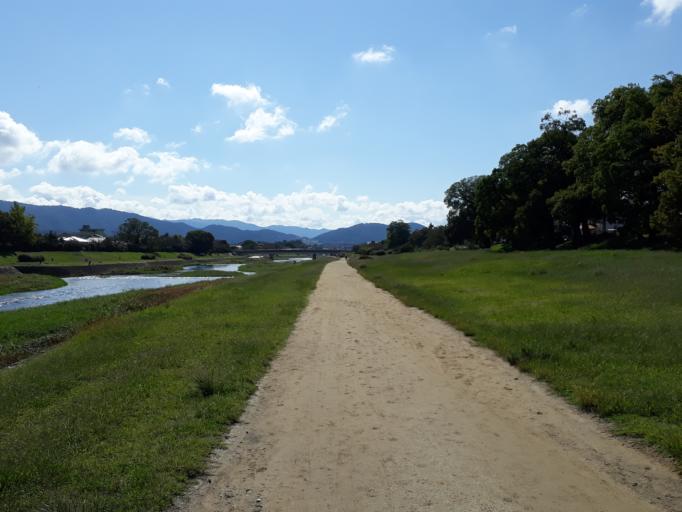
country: JP
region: Kyoto
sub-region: Kyoto-shi
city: Kamigyo-ku
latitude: 35.0421
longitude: 135.7635
